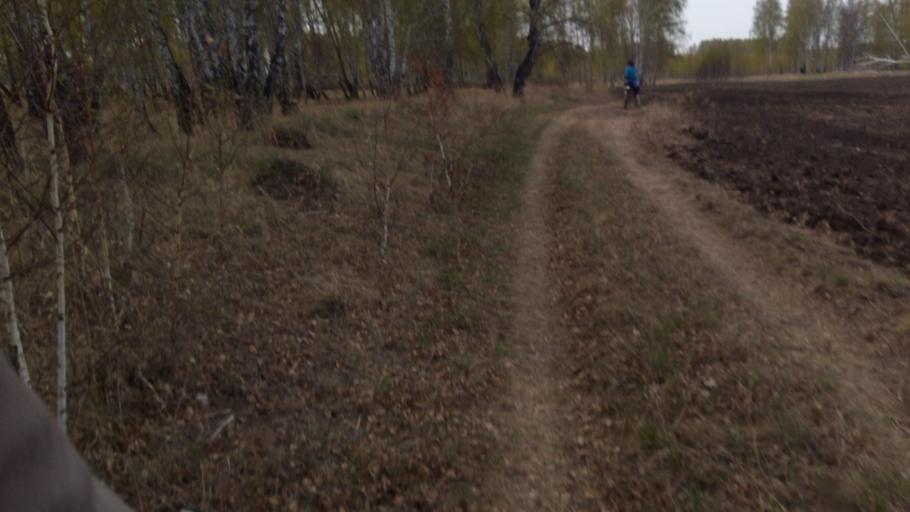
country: RU
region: Chelyabinsk
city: Timiryazevskiy
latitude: 55.0097
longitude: 60.8599
